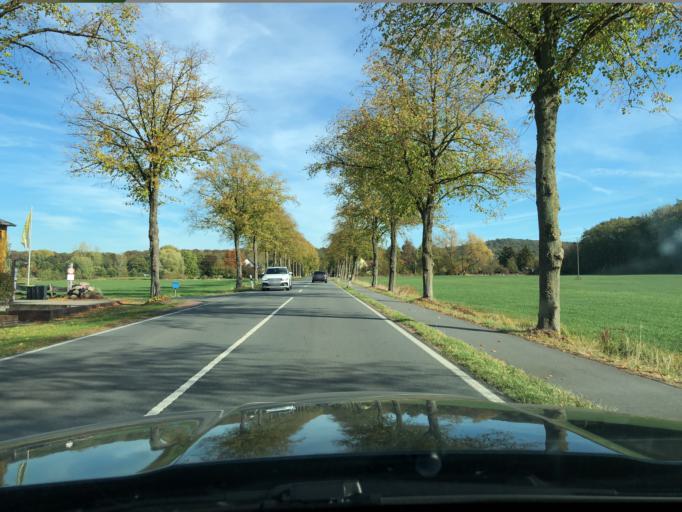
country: DE
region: Lower Saxony
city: Hasbergen
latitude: 52.2182
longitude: 7.9368
